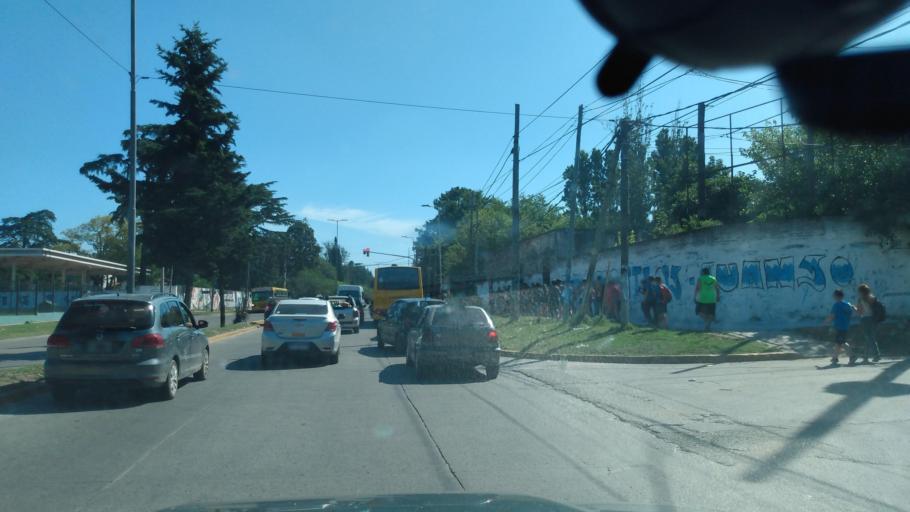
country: AR
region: Buenos Aires
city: Hurlingham
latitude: -34.5567
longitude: -58.7276
